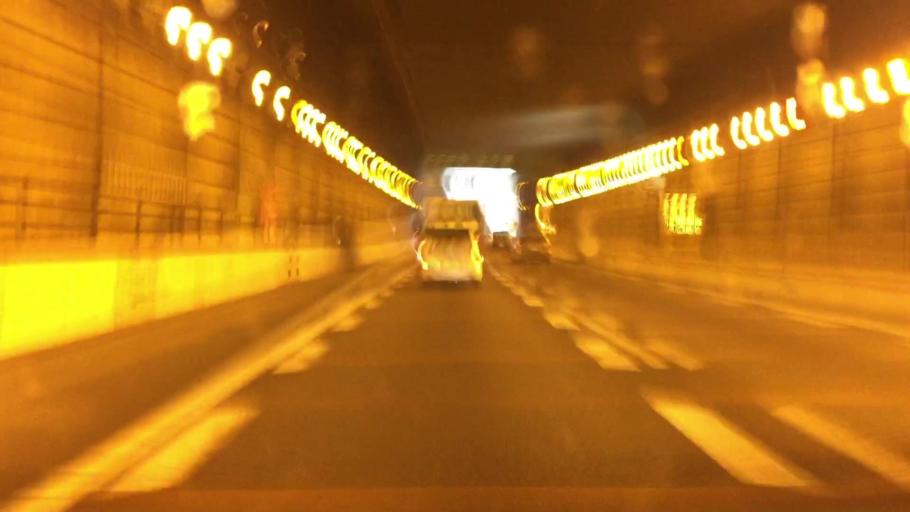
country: JP
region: Saitama
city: Wako
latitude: 35.7662
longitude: 139.6002
